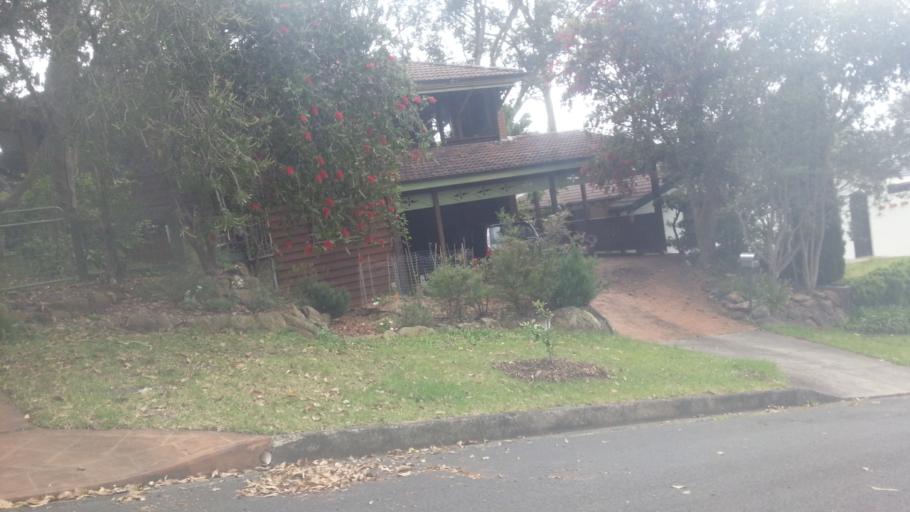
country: AU
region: New South Wales
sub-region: Wollongong
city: Bulli
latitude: -34.3136
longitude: 150.9117
